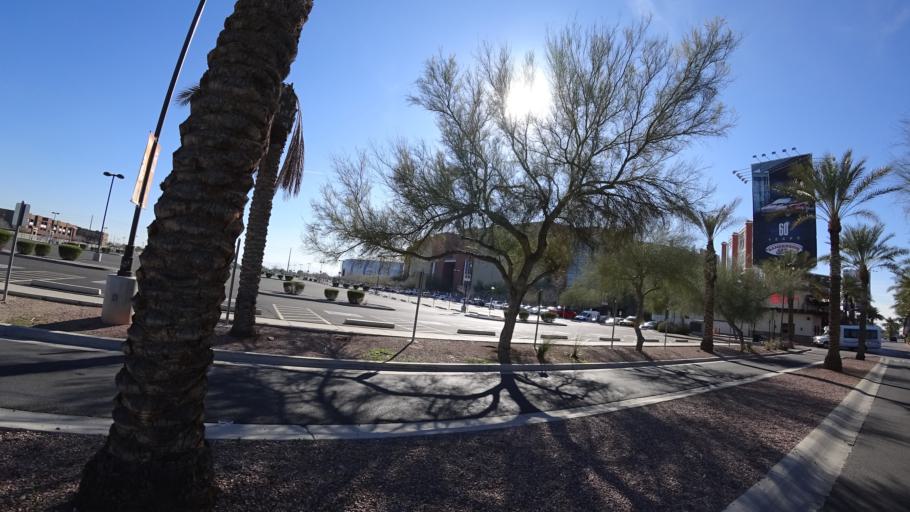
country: US
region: Arizona
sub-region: Maricopa County
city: Peoria
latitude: 33.5332
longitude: -112.2598
